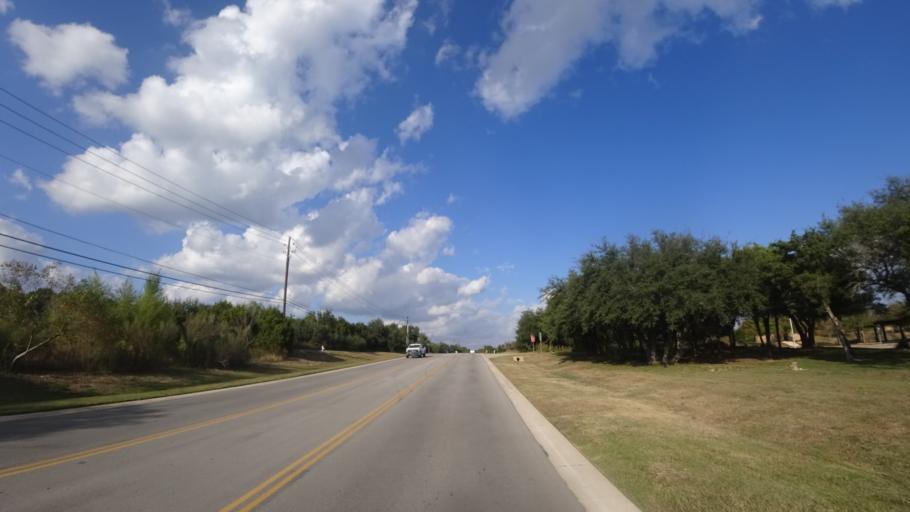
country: US
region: Texas
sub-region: Travis County
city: Barton Creek
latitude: 30.2790
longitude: -97.8841
